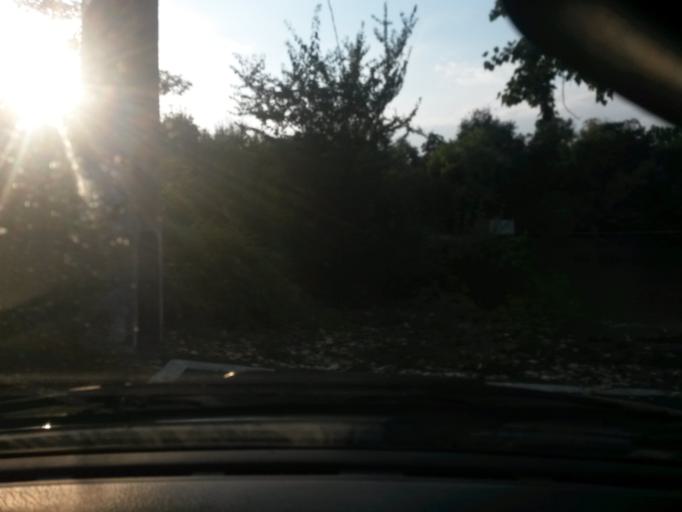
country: RO
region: Mures
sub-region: Comuna Santana de Mures
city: Santana de Mures
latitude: 46.5650
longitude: 24.5705
